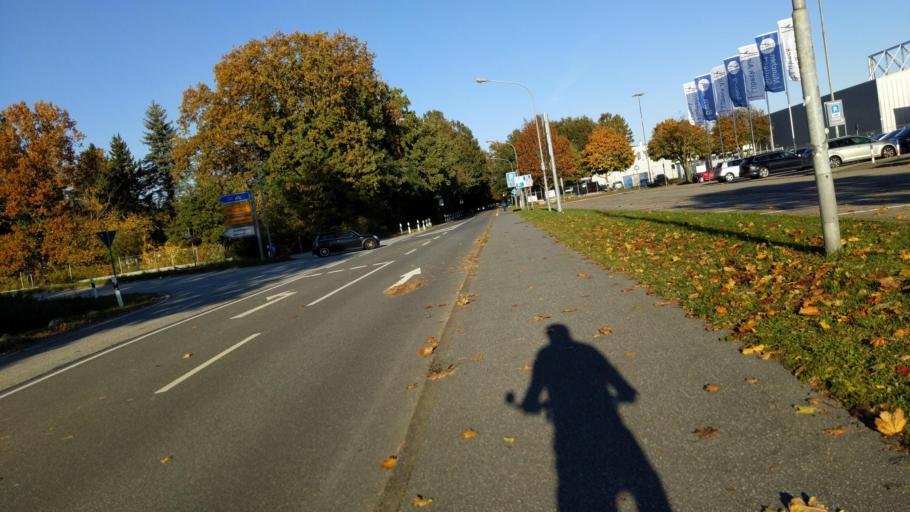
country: DE
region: Schleswig-Holstein
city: Gross Gronau
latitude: 53.8057
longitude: 10.7009
